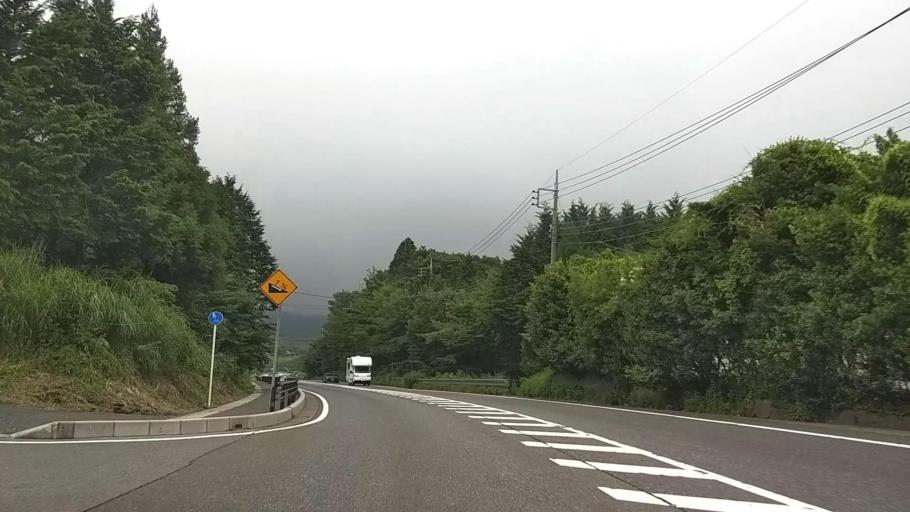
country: JP
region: Yamanashi
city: Fujikawaguchiko
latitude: 35.4270
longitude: 138.5905
